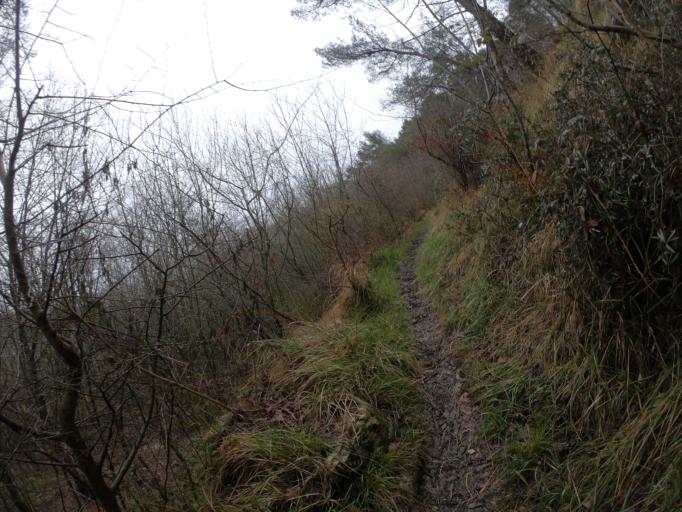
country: IT
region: Liguria
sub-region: Provincia di Imperia
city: Villa Faraldi
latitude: 43.9747
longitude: 8.1032
